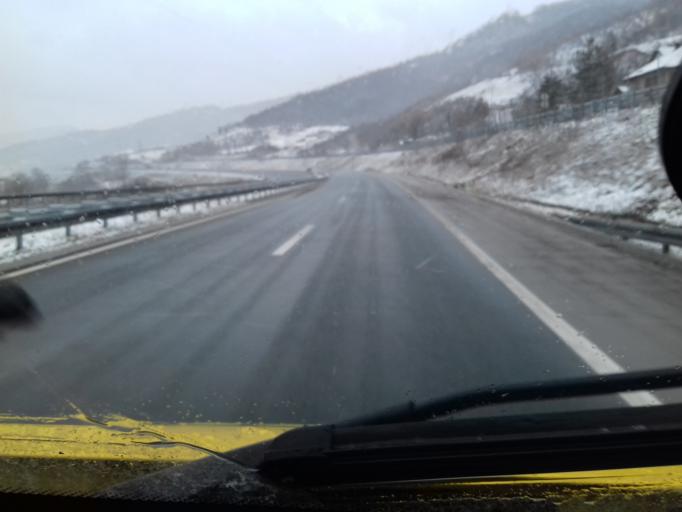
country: BA
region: Federation of Bosnia and Herzegovina
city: Kakanj
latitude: 44.1351
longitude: 18.0506
